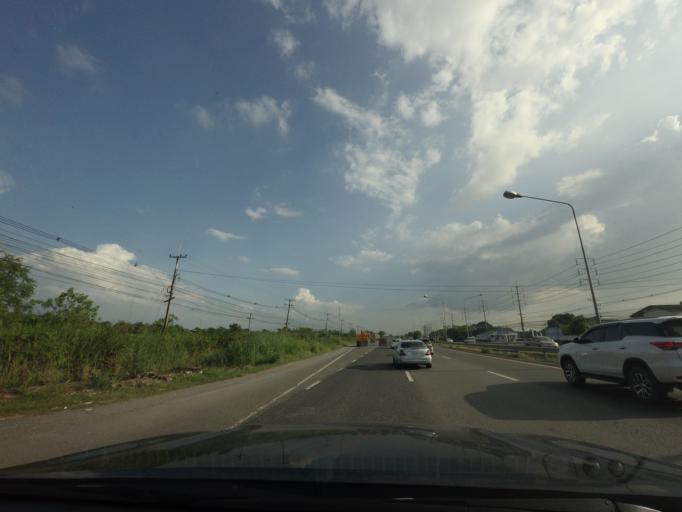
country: TH
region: Sara Buri
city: Saraburi
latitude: 14.5697
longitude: 100.9033
